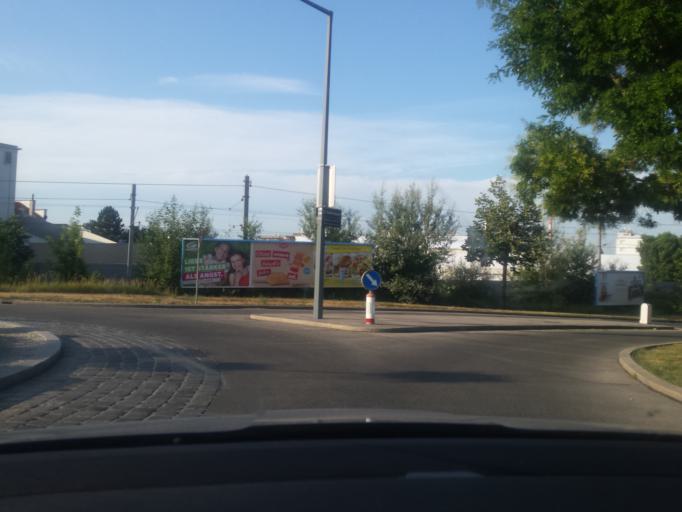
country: AT
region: Lower Austria
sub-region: Politischer Bezirk Wien-Umgebung
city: Leopoldsdorf
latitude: 48.1667
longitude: 16.4107
